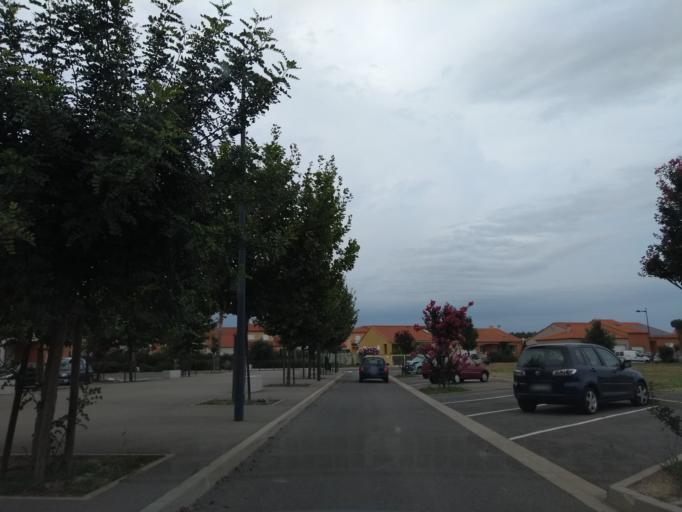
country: FR
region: Languedoc-Roussillon
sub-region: Departement des Pyrenees-Orientales
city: Elne
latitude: 42.6115
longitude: 2.9717
